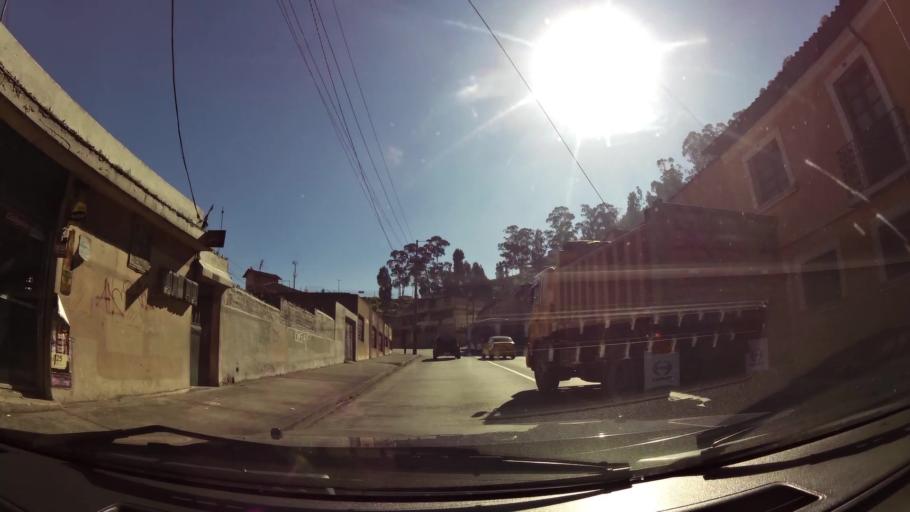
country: EC
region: Pichincha
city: Quito
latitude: -0.2296
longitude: -78.5223
